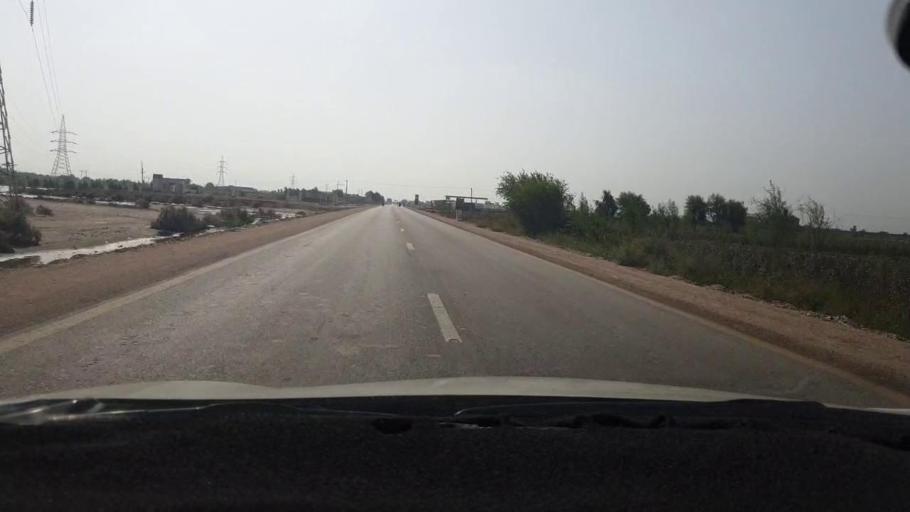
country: PK
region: Sindh
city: Jhol
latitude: 25.9244
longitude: 69.0009
